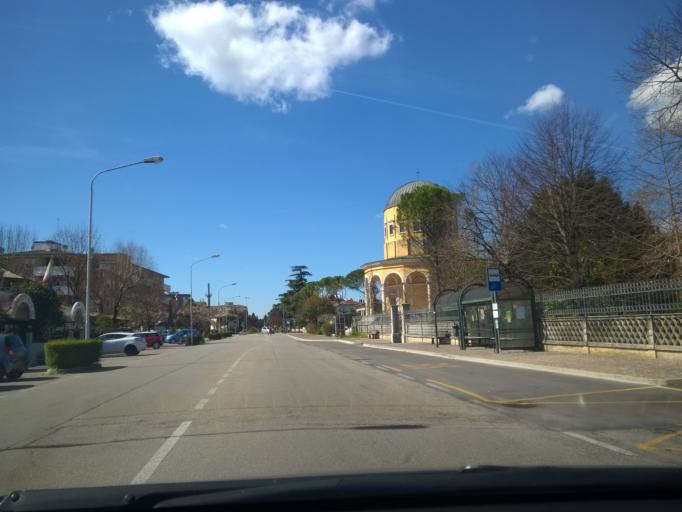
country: IT
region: Friuli Venezia Giulia
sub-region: Provincia di Pordenone
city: Sacile
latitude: 45.9597
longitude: 12.5095
